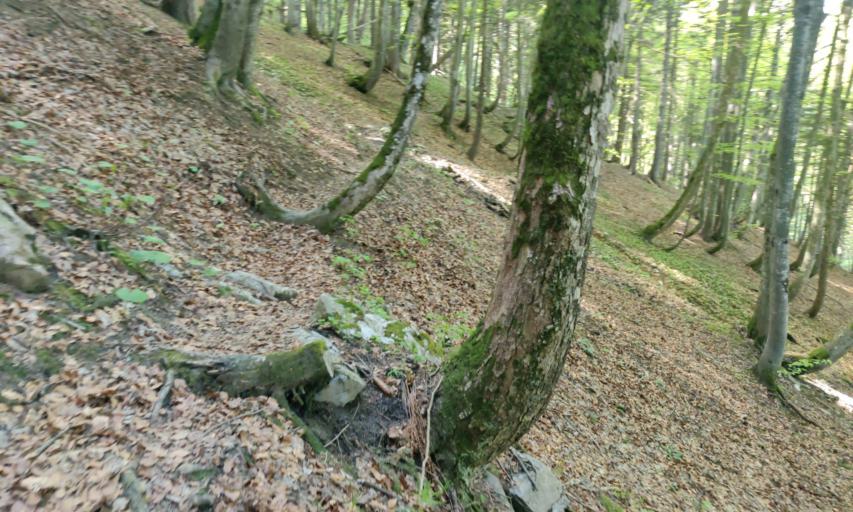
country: CH
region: Saint Gallen
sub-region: Wahlkreis Sarganserland
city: Sargans
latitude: 47.0736
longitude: 9.4424
